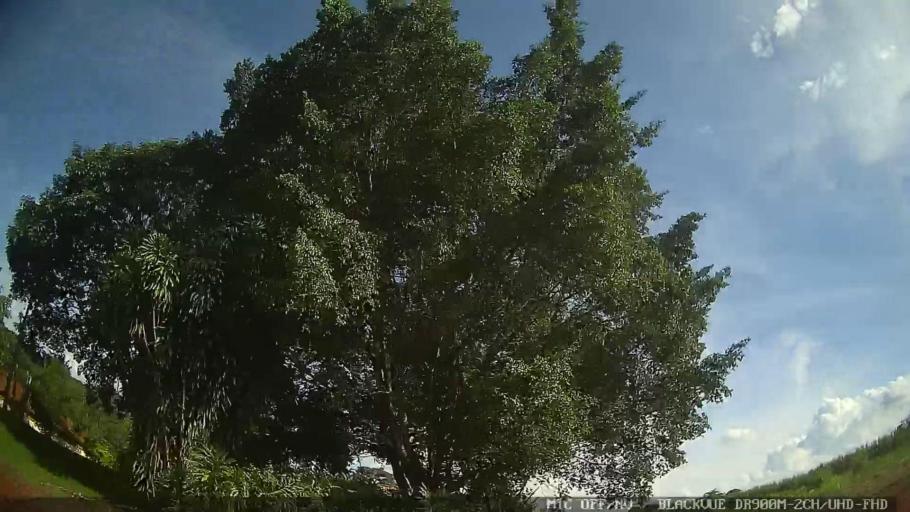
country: BR
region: Sao Paulo
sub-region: Jaguariuna
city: Jaguariuna
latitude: -22.6461
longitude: -47.0677
